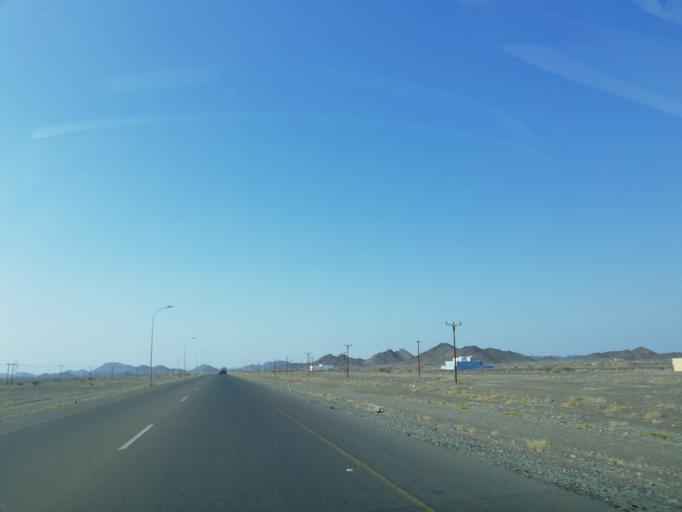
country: OM
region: Ash Sharqiyah
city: Ibra'
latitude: 22.7613
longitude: 58.1459
